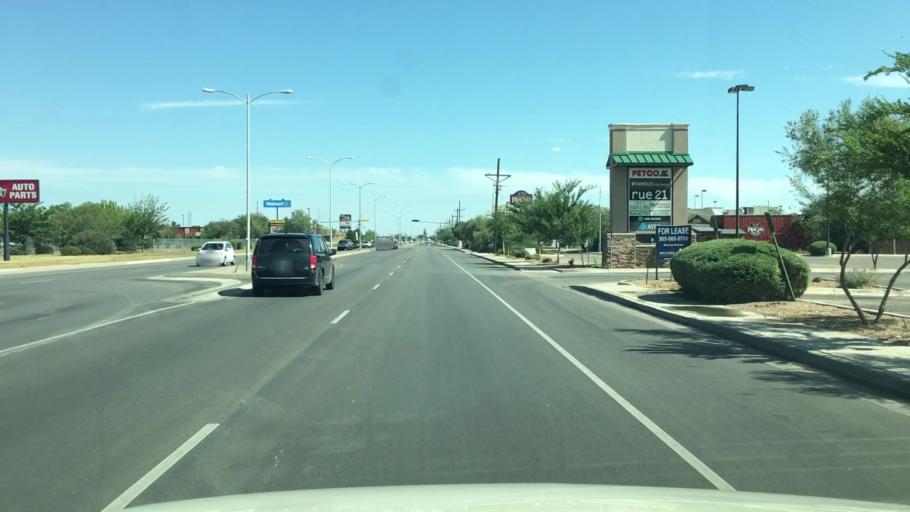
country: US
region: New Mexico
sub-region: Chaves County
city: Roswell
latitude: 33.4469
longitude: -104.5232
